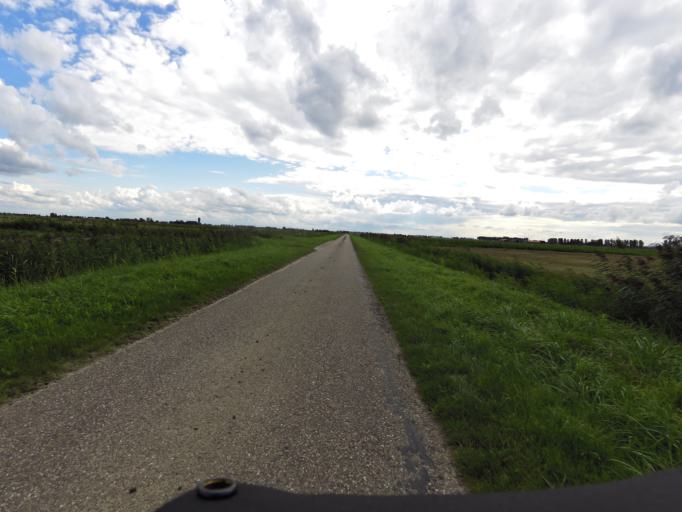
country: NL
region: South Holland
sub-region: Gemeente Goeree-Overflakkee
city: Middelharnis
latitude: 51.7161
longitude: 4.2428
